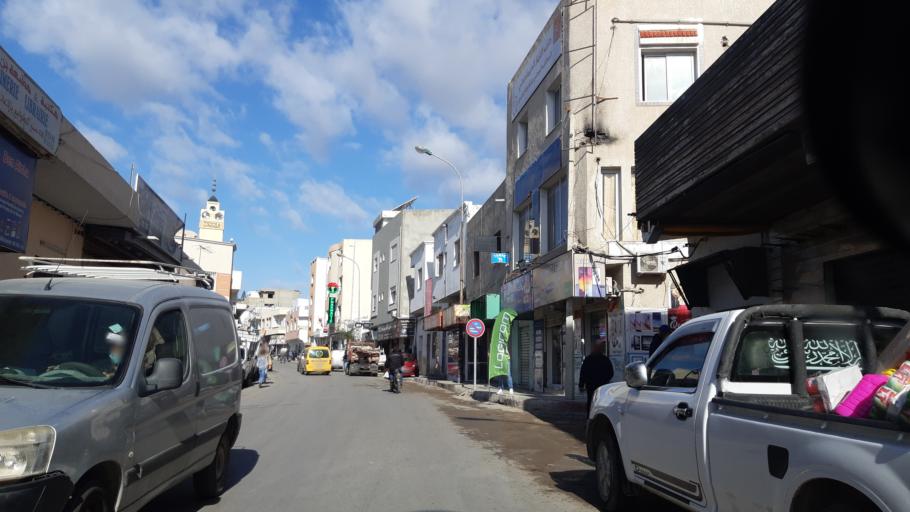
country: TN
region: Susah
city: Akouda
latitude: 35.8700
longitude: 10.5382
